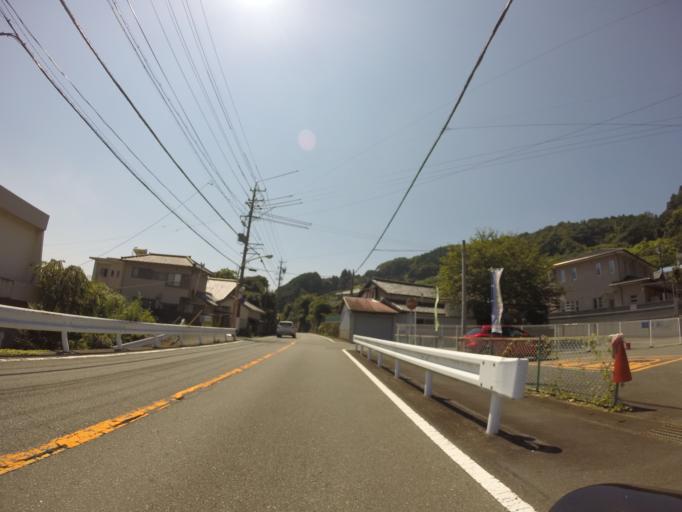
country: JP
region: Shizuoka
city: Fujinomiya
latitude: 35.1719
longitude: 138.6162
